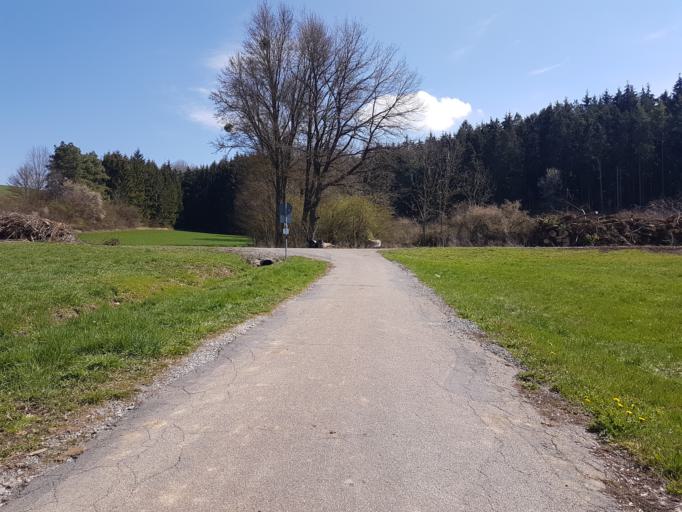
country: DE
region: Baden-Wuerttemberg
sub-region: Karlsruhe Region
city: Rosenberg
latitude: 49.3883
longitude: 9.5016
